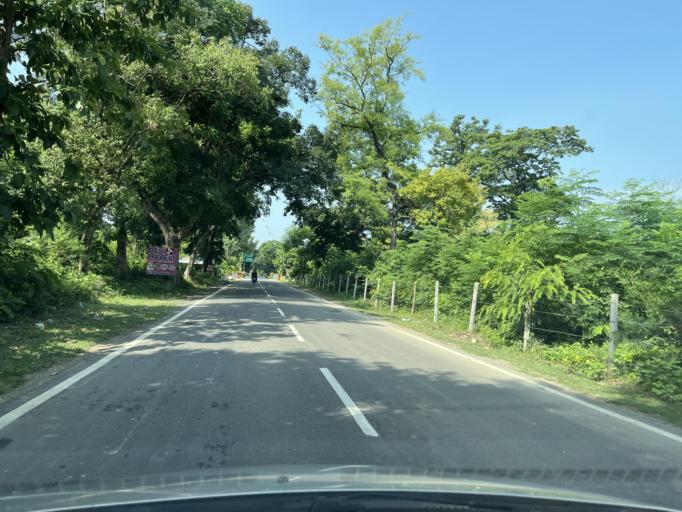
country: IN
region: Uttarakhand
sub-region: Naini Tal
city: Kaladhungi
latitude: 29.2201
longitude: 79.2336
